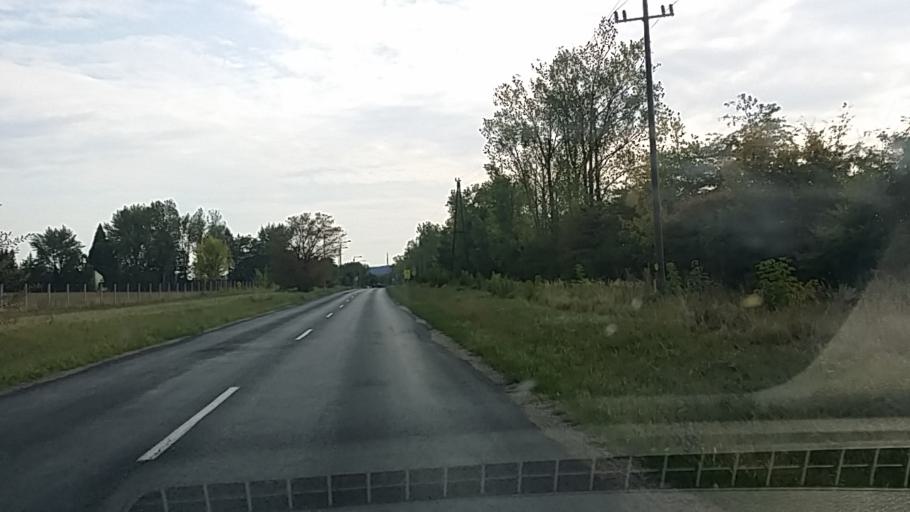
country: HU
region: Gyor-Moson-Sopron
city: Fertorakos
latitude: 47.7211
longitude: 16.6188
